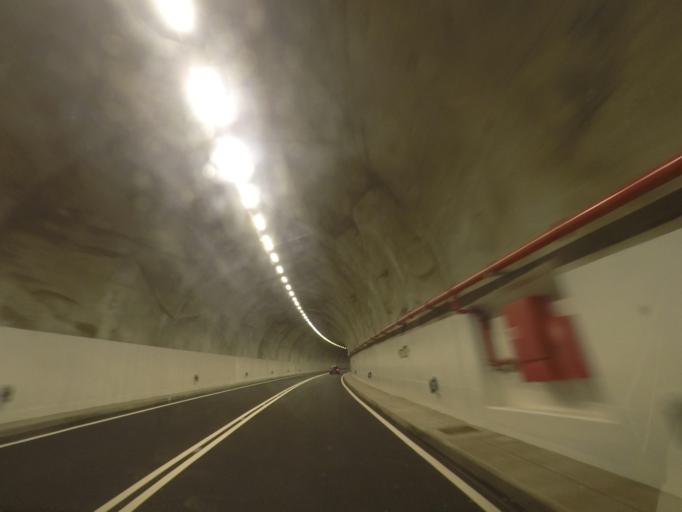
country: PT
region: Madeira
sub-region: Santana
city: Santana
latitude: 32.8175
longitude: -16.9029
